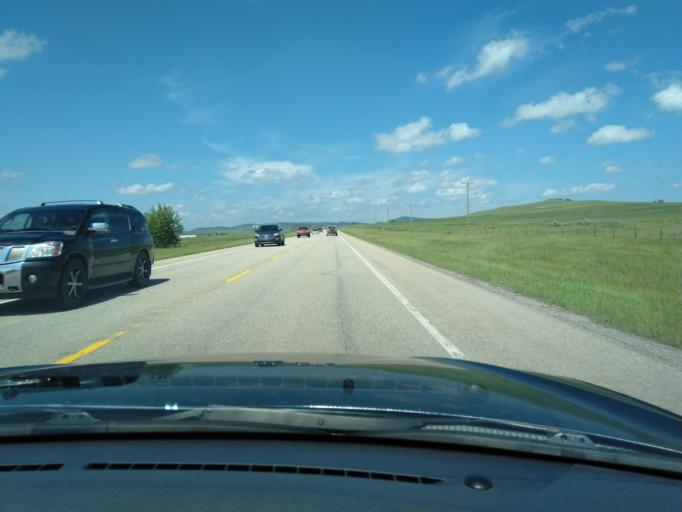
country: CA
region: Alberta
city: Cochrane
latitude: 51.2112
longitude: -114.5261
